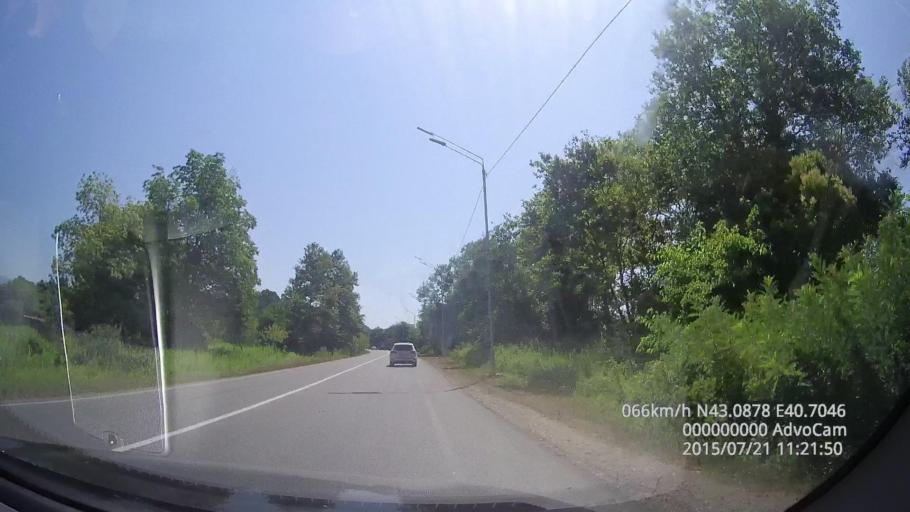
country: GE
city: P'rimorsk'oe
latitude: 43.0874
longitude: 40.7046
